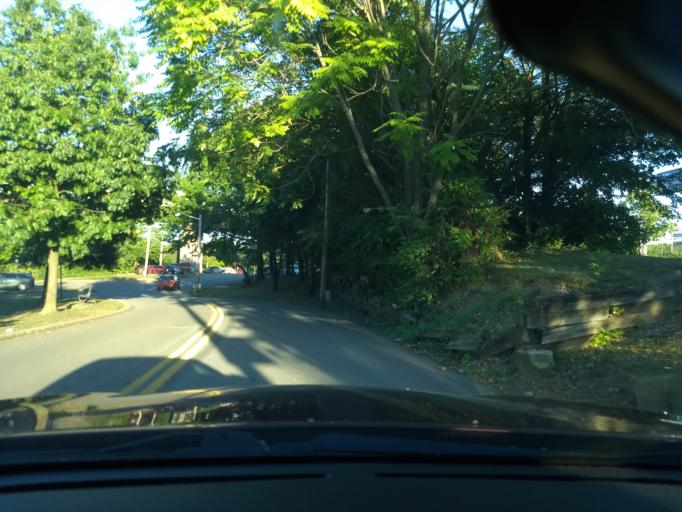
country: US
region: Pennsylvania
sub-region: Allegheny County
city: Mount Oliver
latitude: 40.4322
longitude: -79.9754
